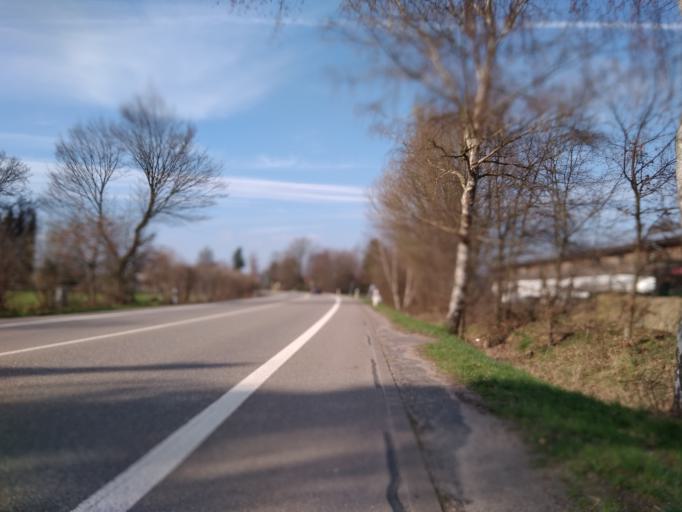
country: DE
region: North Rhine-Westphalia
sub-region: Regierungsbezirk Munster
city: Gladbeck
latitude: 51.5908
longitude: 6.9319
